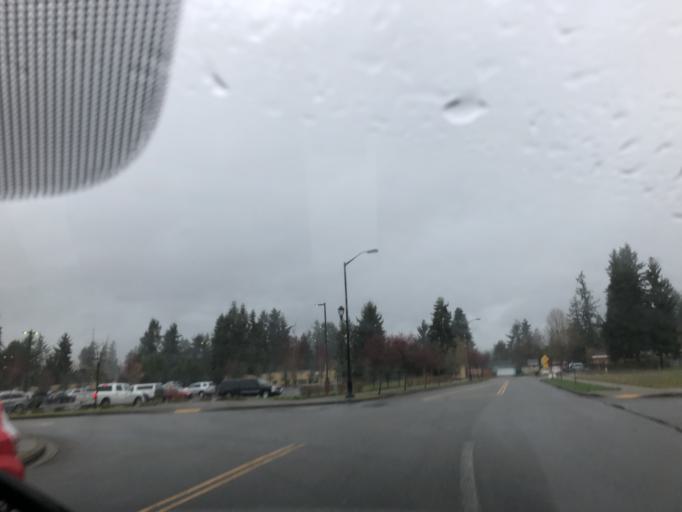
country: US
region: Washington
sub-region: Thurston County
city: Tanglewilde-Thompson Place
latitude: 47.0548
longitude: -122.7778
